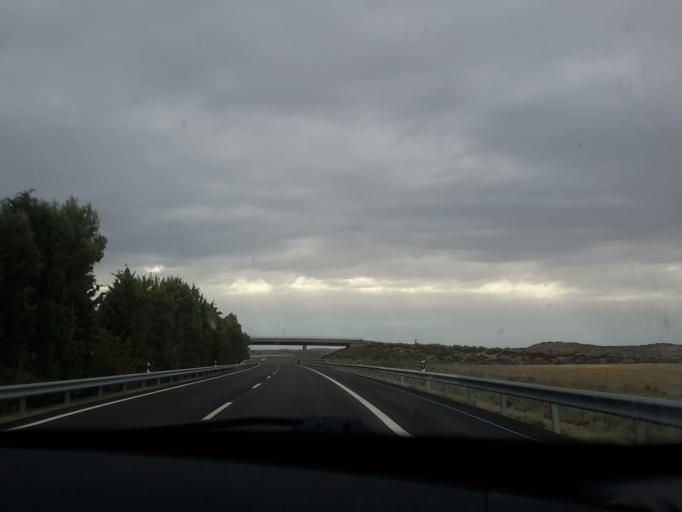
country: ES
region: Aragon
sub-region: Provincia de Huesca
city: Castejon de Monegros
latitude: 41.5250
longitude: -0.3257
